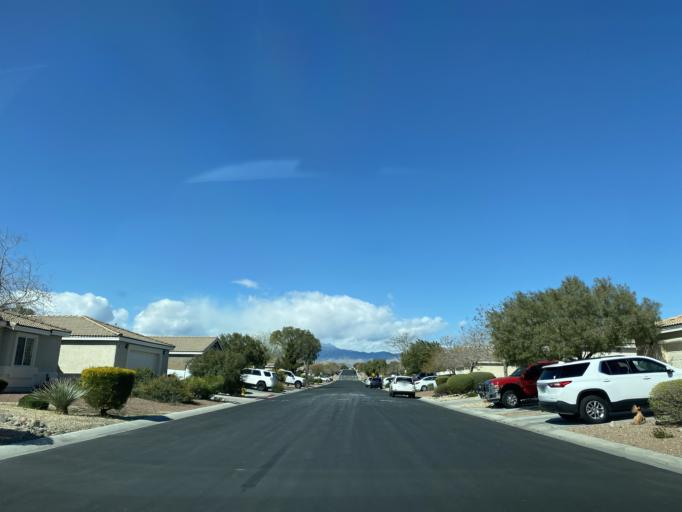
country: US
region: Nevada
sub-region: Clark County
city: North Las Vegas
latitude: 36.3291
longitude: -115.2665
